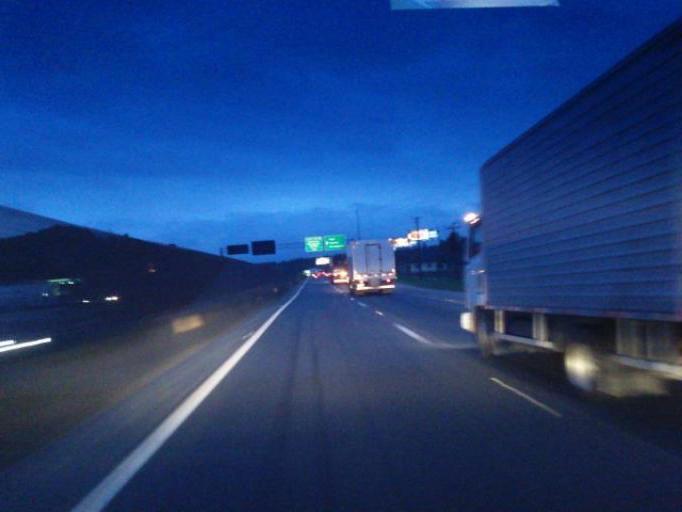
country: BR
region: Santa Catarina
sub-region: Navegantes
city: Navegantes
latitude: -26.8348
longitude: -48.7038
